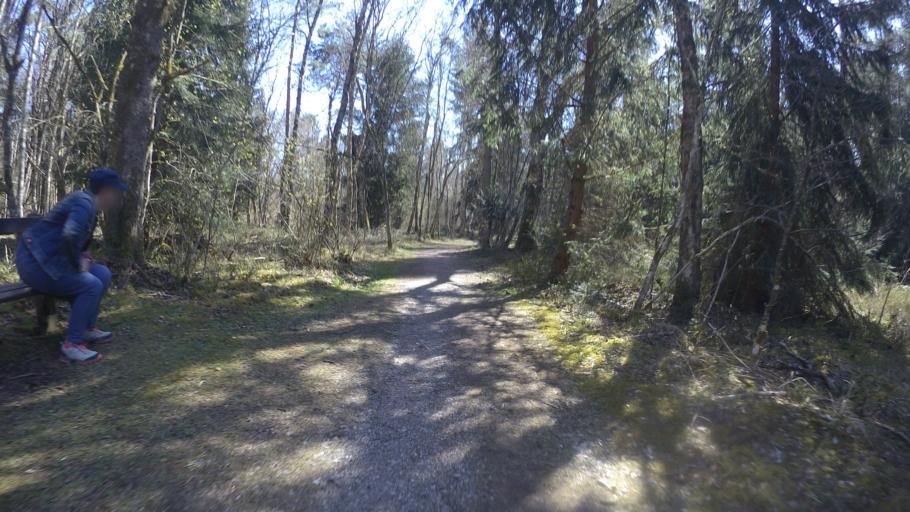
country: DE
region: Bavaria
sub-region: Upper Bavaria
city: Seeon-Seebruck
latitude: 47.9349
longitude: 12.4867
